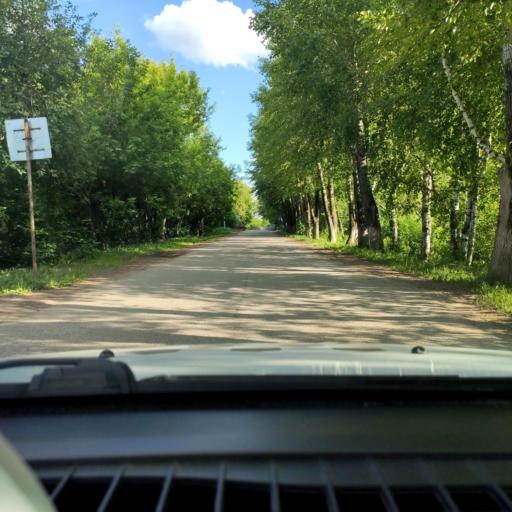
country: RU
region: Perm
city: Ferma
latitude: 57.9024
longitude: 56.3018
